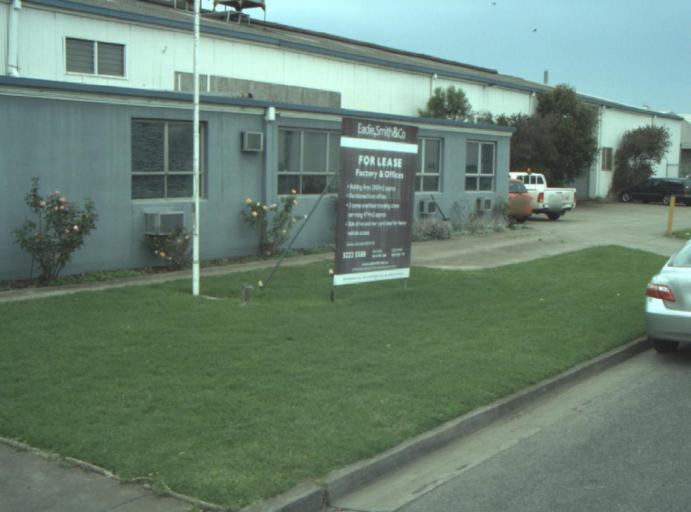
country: AU
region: Victoria
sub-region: Greater Geelong
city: Breakwater
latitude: -38.1840
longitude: 144.3665
